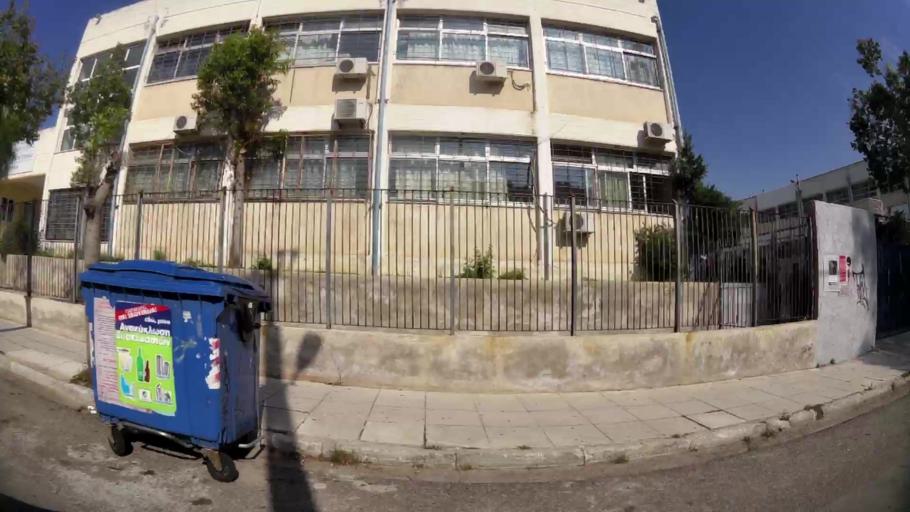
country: GR
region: Attica
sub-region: Nomos Piraios
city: Drapetsona
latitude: 37.9507
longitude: 23.6199
